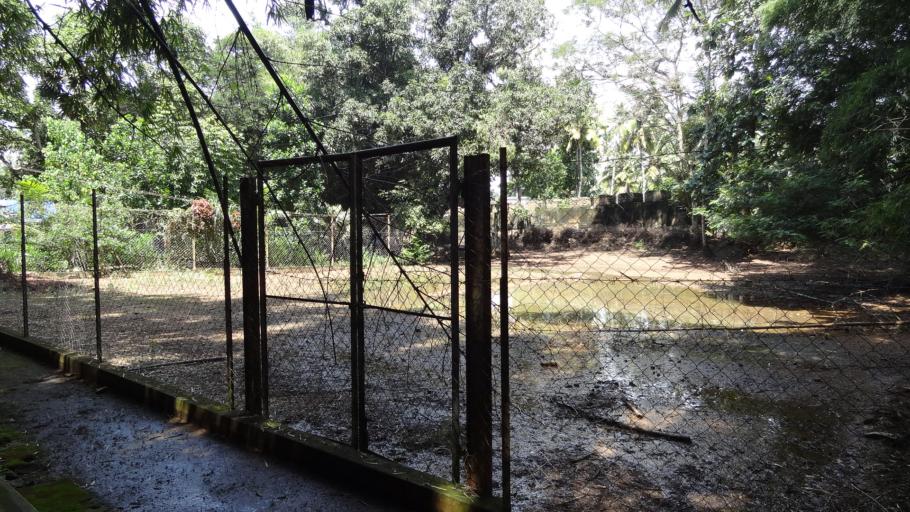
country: IN
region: Tamil Nadu
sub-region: Kanniyakumari
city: Padmanabhapuram
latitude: 8.2429
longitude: 77.3354
